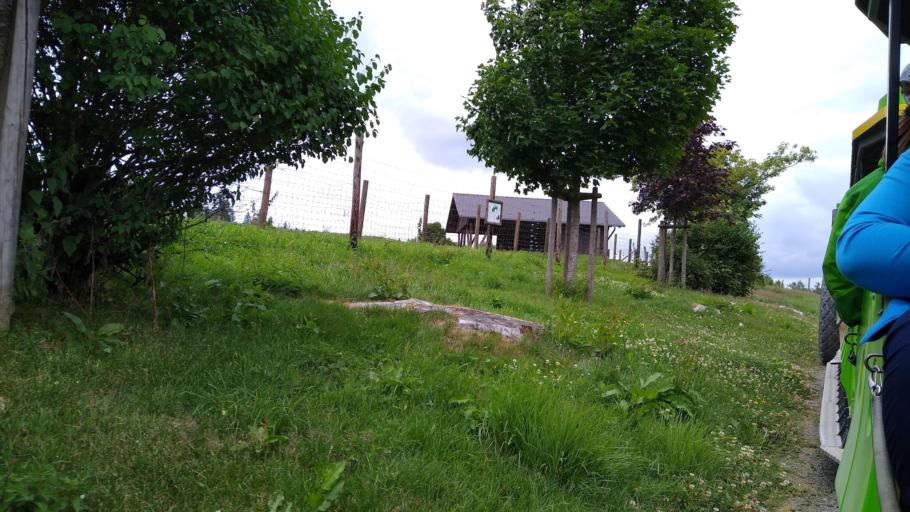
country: DE
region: North Rhine-Westphalia
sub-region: Regierungsbezirk Arnsberg
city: Kirchhundem
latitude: 51.0620
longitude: 8.1806
